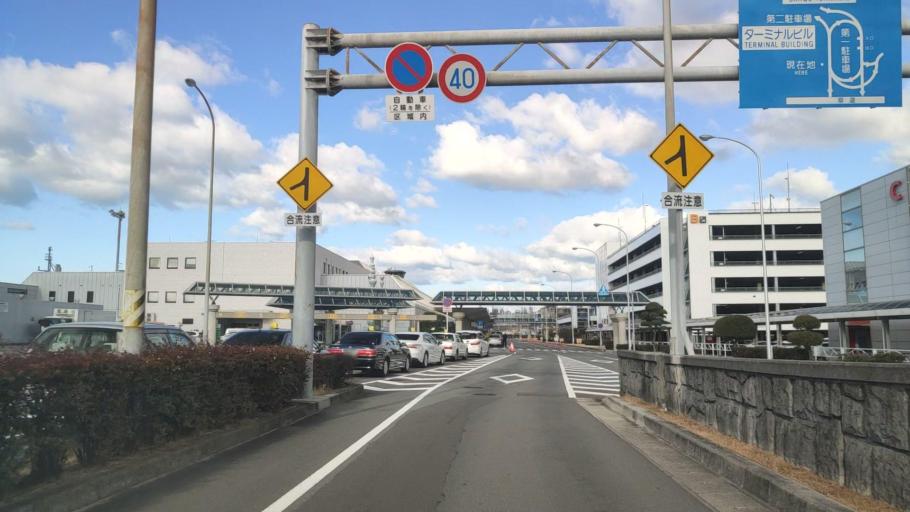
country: JP
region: Ehime
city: Masaki-cho
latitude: 33.8282
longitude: 132.7059
